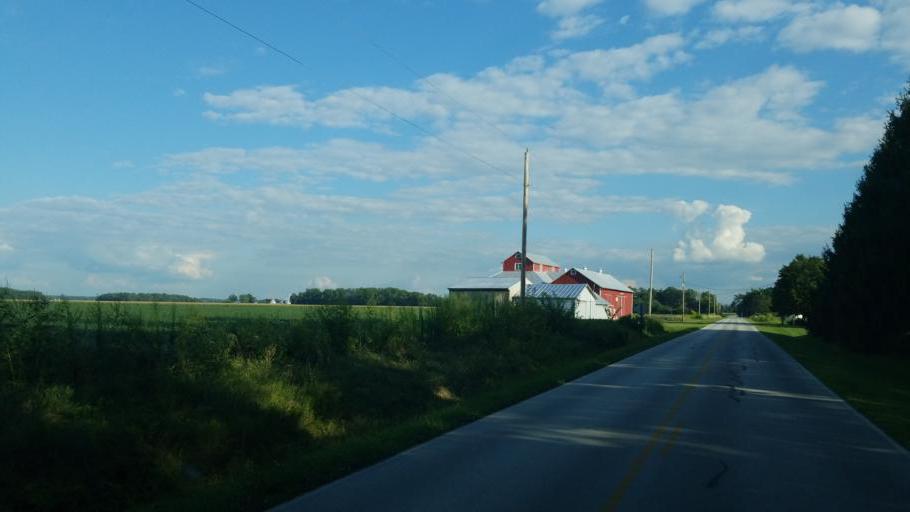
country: US
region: Ohio
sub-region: Sandusky County
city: Green Springs
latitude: 41.2241
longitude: -83.1282
